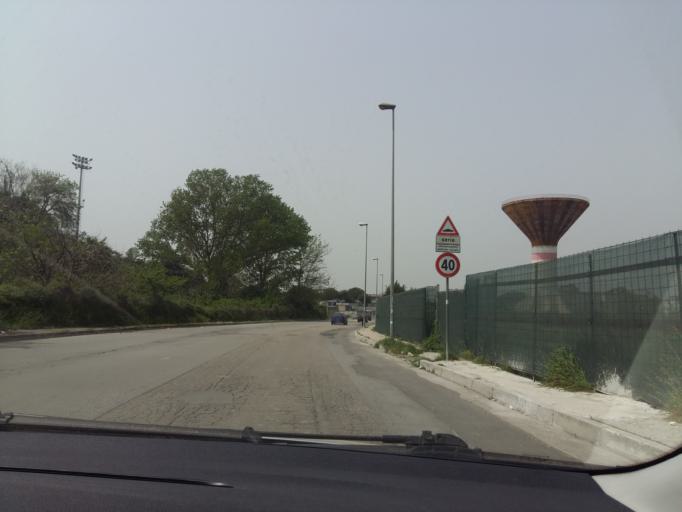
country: IT
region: Campania
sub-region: Provincia di Napoli
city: Mugnano di Napoli
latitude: 40.9000
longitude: 14.2040
